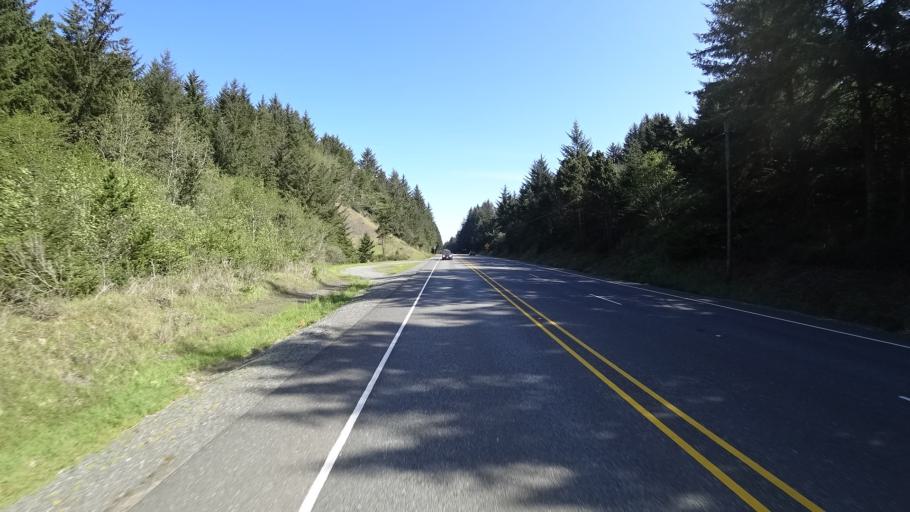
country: US
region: Oregon
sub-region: Curry County
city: Brookings
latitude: 42.1174
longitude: -124.3489
